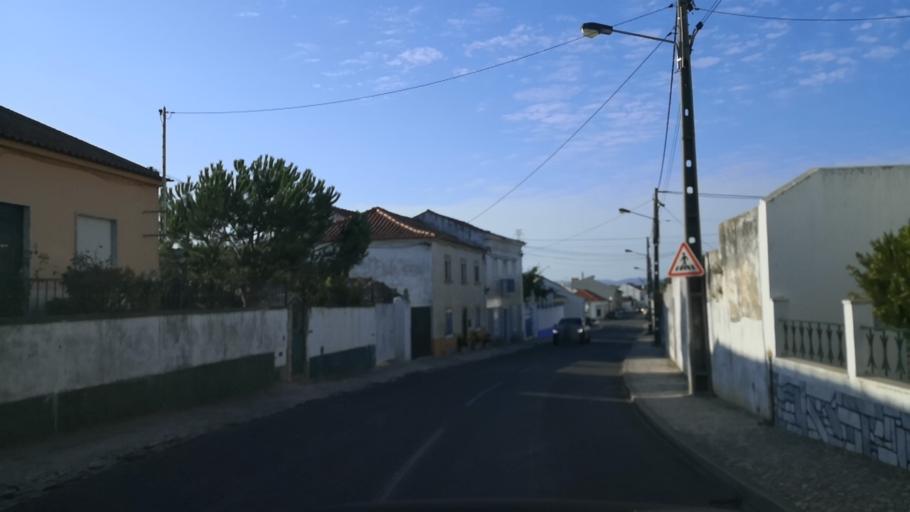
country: PT
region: Santarem
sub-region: Santarem
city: Santarem
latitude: 39.2991
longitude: -8.6607
